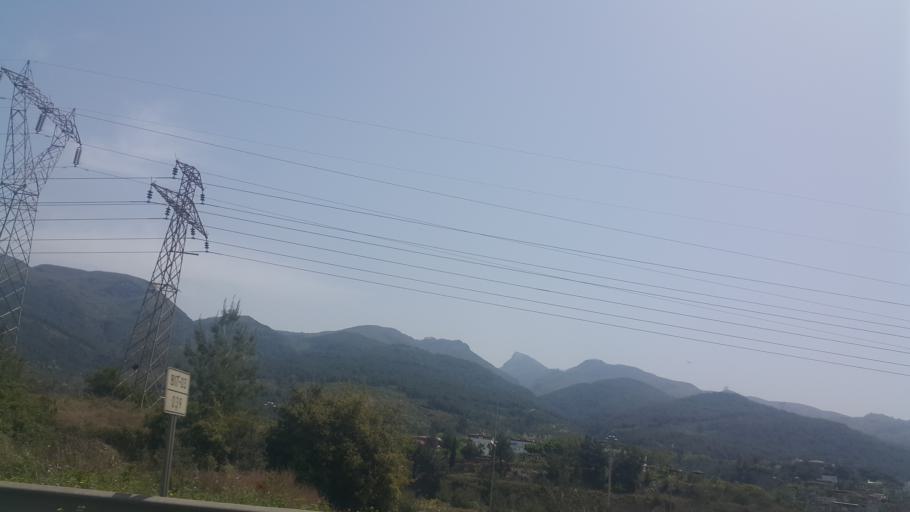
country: TR
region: Hatay
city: Yakacik
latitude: 36.7139
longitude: 36.2202
